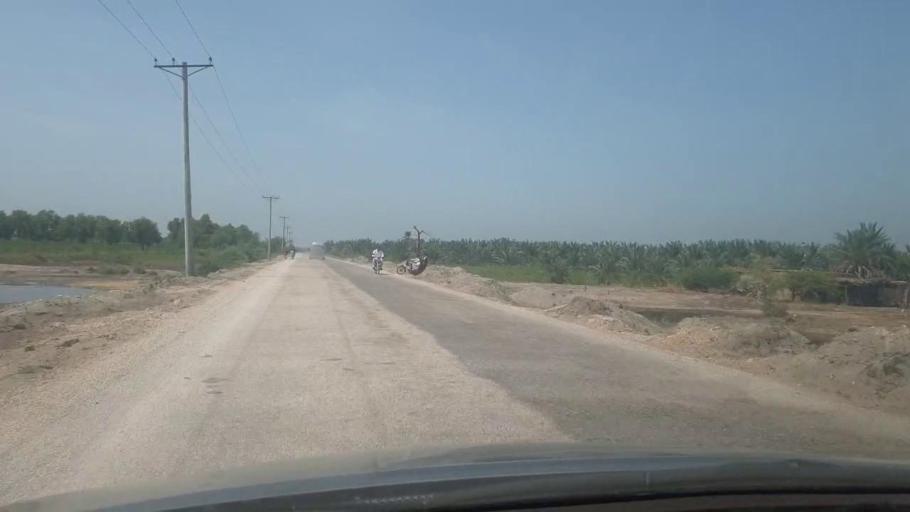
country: PK
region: Sindh
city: Ranipur
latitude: 27.2708
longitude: 68.5951
